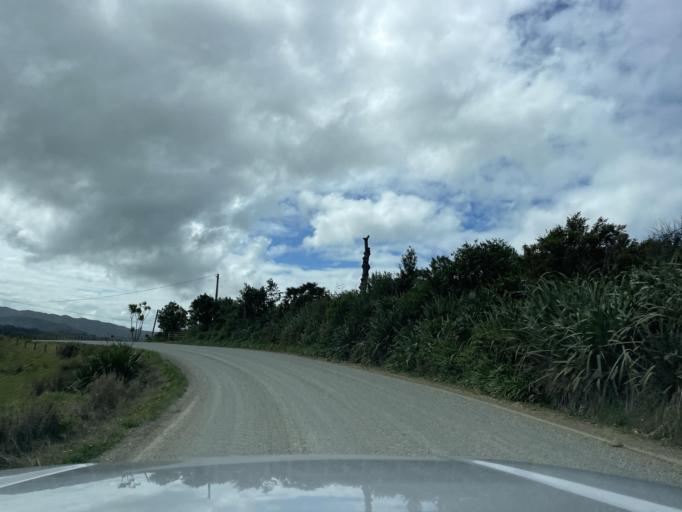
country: NZ
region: Auckland
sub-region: Auckland
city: Wellsford
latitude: -36.1350
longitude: 174.5364
